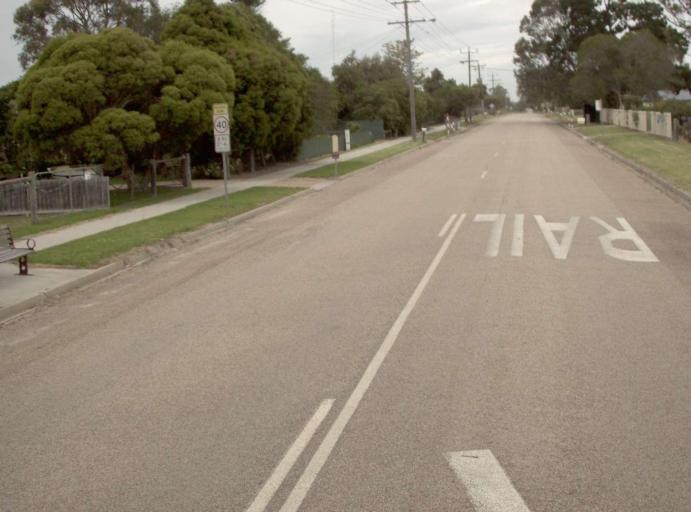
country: AU
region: Victoria
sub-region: East Gippsland
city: Bairnsdale
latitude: -37.8261
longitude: 147.4344
